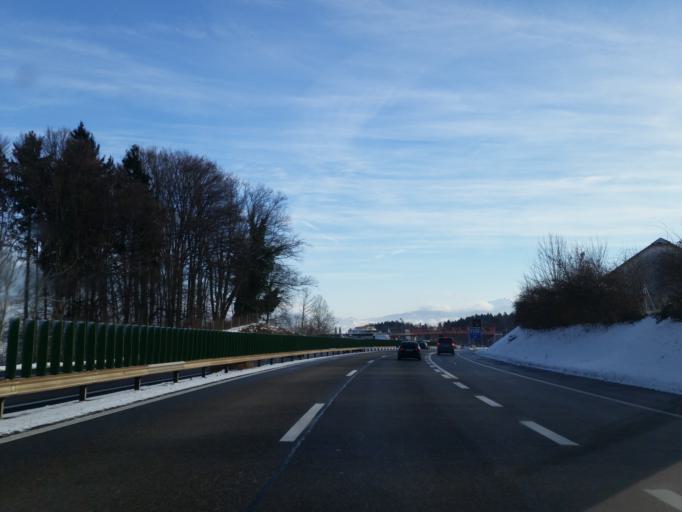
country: CH
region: Schwyz
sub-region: Bezirk Hoefe
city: Feusisberg
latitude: 47.1954
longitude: 8.7479
